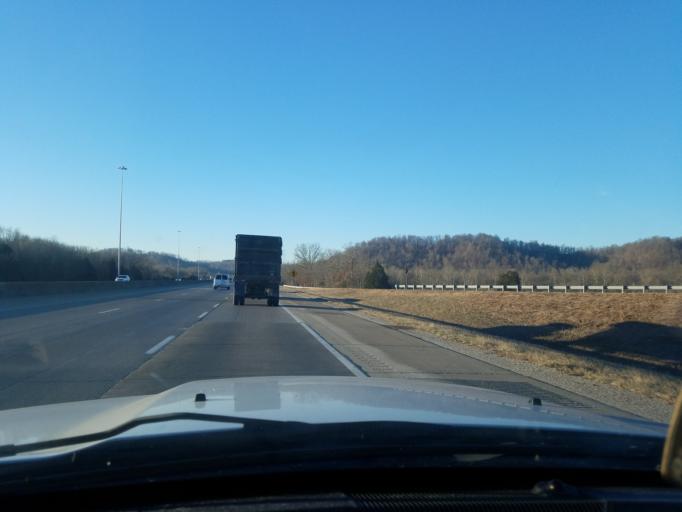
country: US
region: Kentucky
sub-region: Bullitt County
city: Lebanon Junction
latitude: 37.8024
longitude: -85.7490
